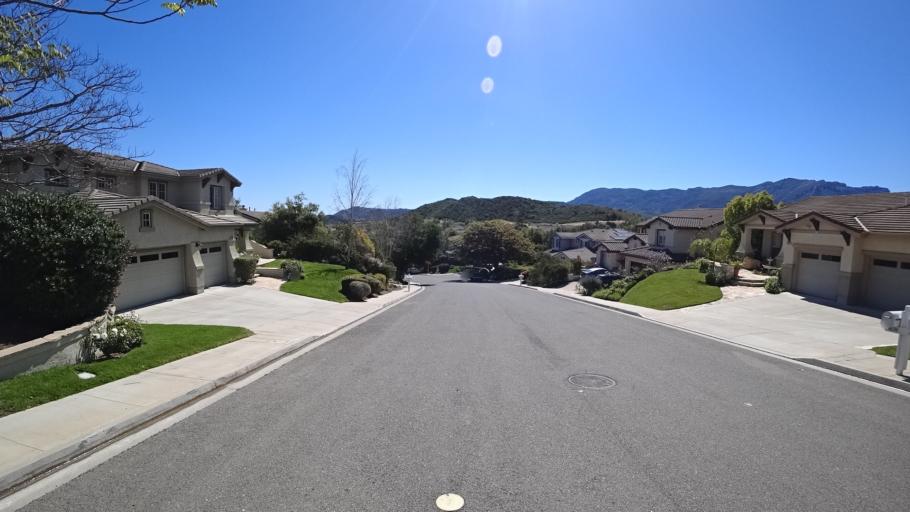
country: US
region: California
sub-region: Ventura County
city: Casa Conejo
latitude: 34.1663
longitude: -118.9743
